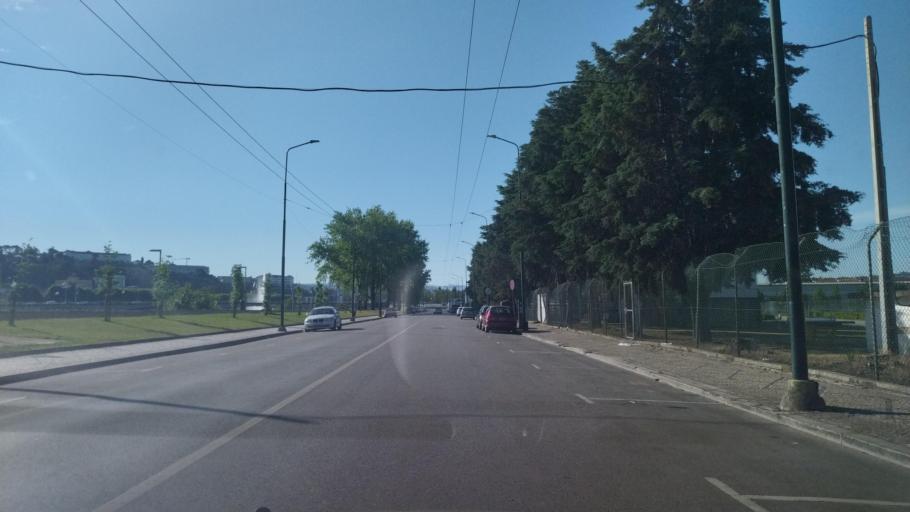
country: PT
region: Coimbra
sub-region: Coimbra
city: Coimbra
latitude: 40.2074
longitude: -8.4343
